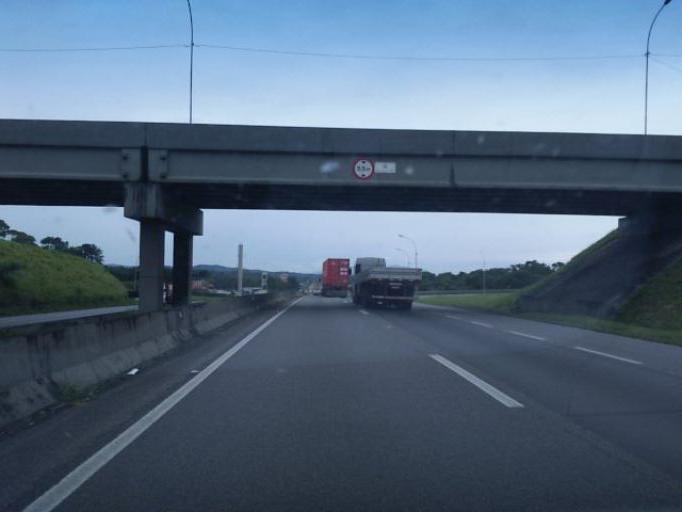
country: BR
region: Sao Paulo
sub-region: Pariquera-Acu
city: Pariquera Acu
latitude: -24.6197
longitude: -47.8927
